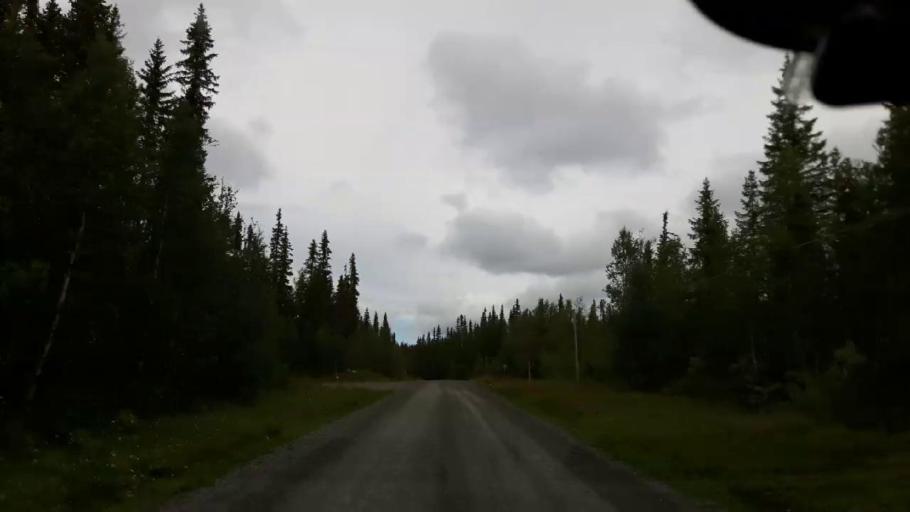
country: SE
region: Jaemtland
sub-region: Krokoms Kommun
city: Valla
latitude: 63.7097
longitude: 13.8633
